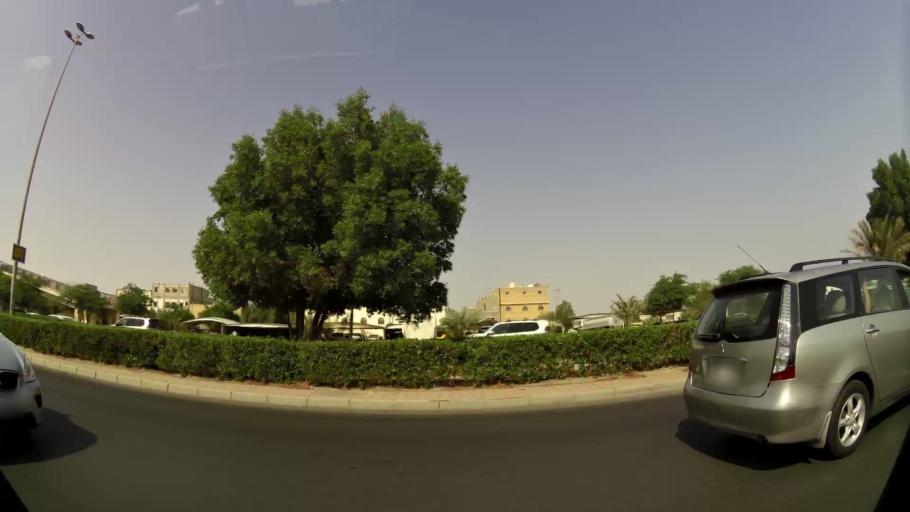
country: KW
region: Muhafazat al Jahra'
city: Al Jahra'
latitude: 29.3367
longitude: 47.6620
